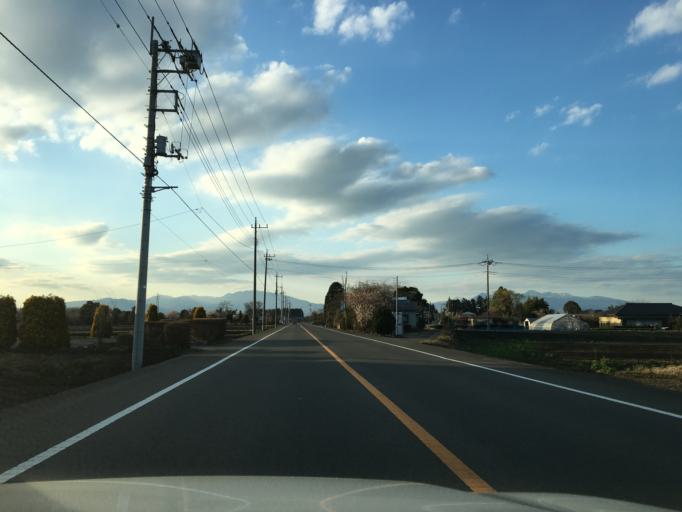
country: JP
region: Tochigi
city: Otawara
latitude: 36.8789
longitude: 140.0670
